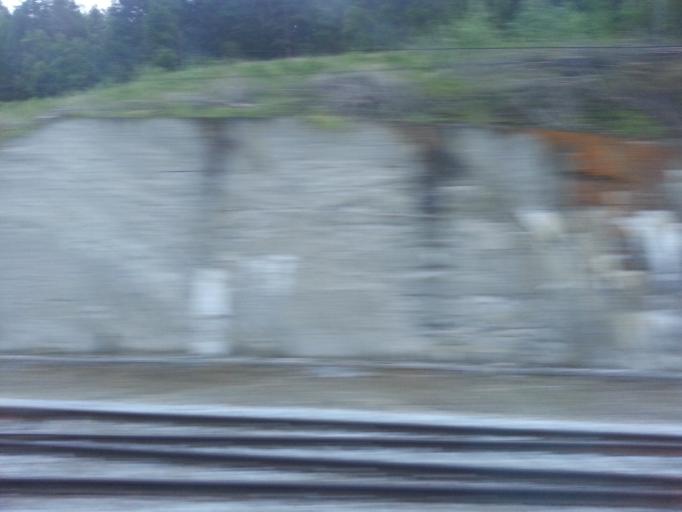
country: NO
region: Oppland
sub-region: Dovre
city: Dombas
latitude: 62.0654
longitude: 9.1241
